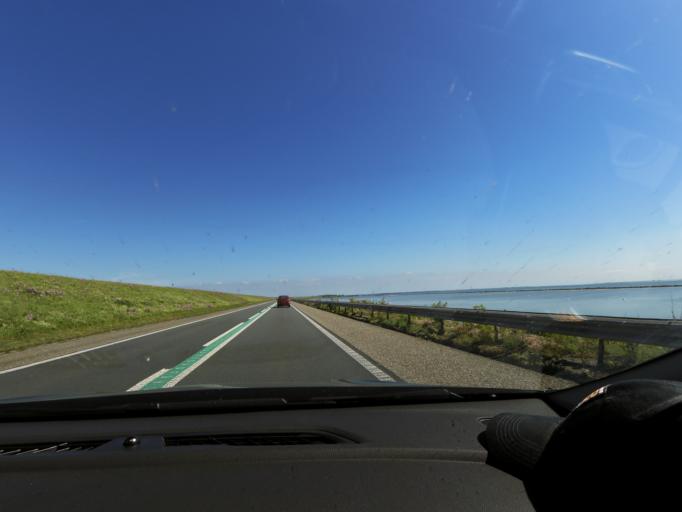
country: NL
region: North Holland
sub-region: Gemeente Enkhuizen
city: Enkhuizen
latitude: 52.6533
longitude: 5.3927
